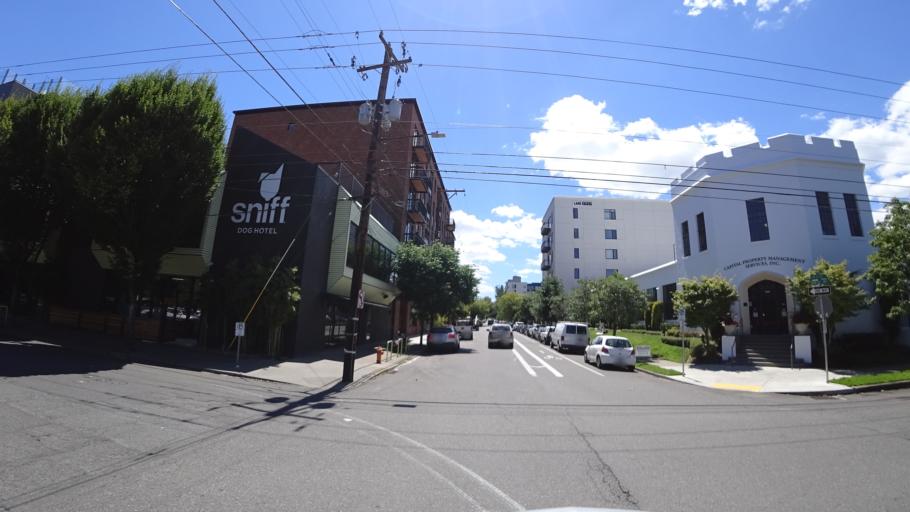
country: US
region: Oregon
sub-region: Multnomah County
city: Portland
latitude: 45.5343
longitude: -122.6906
